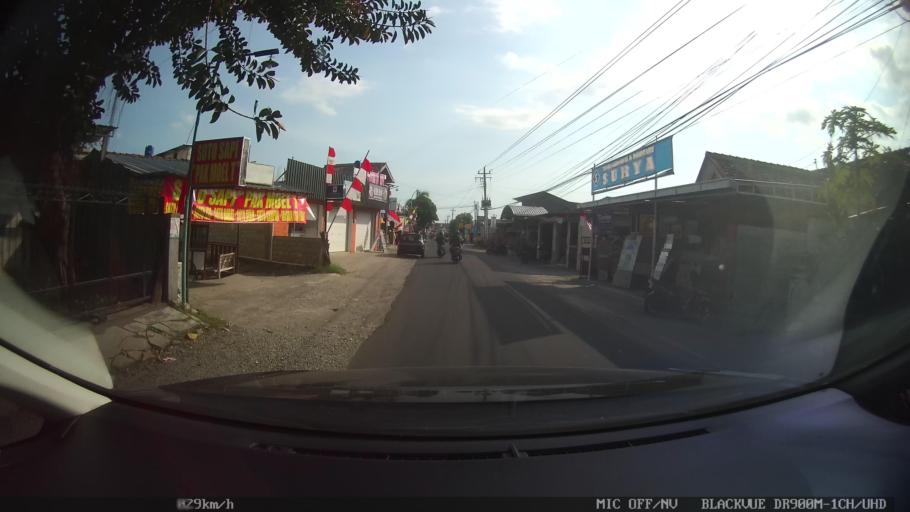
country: ID
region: Daerah Istimewa Yogyakarta
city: Kasihan
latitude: -7.8264
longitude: 110.3269
